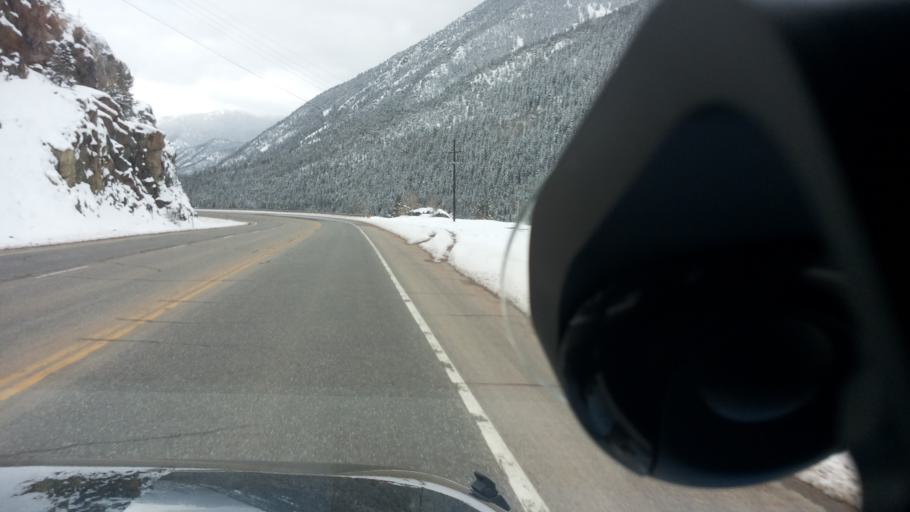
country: US
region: Colorado
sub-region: Clear Creek County
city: Georgetown
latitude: 39.7643
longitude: -105.7424
